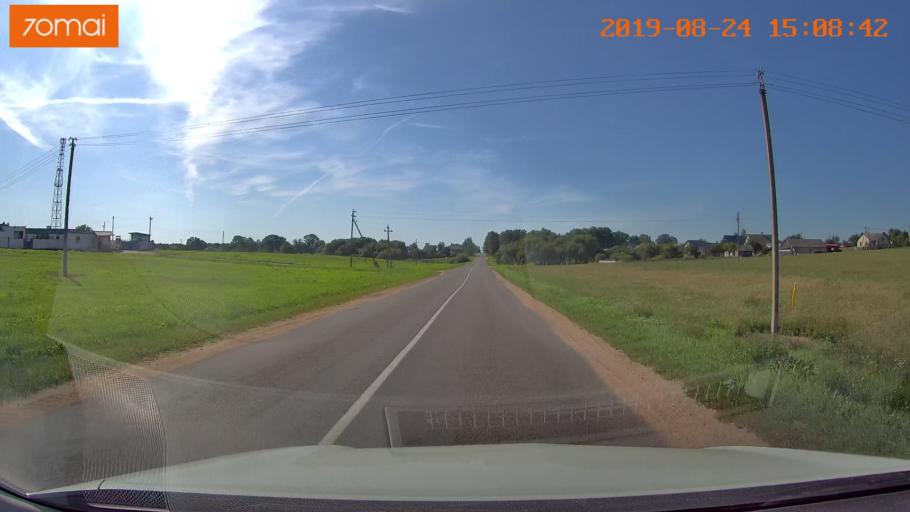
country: BY
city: Michanovichi
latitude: 53.6083
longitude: 27.6511
